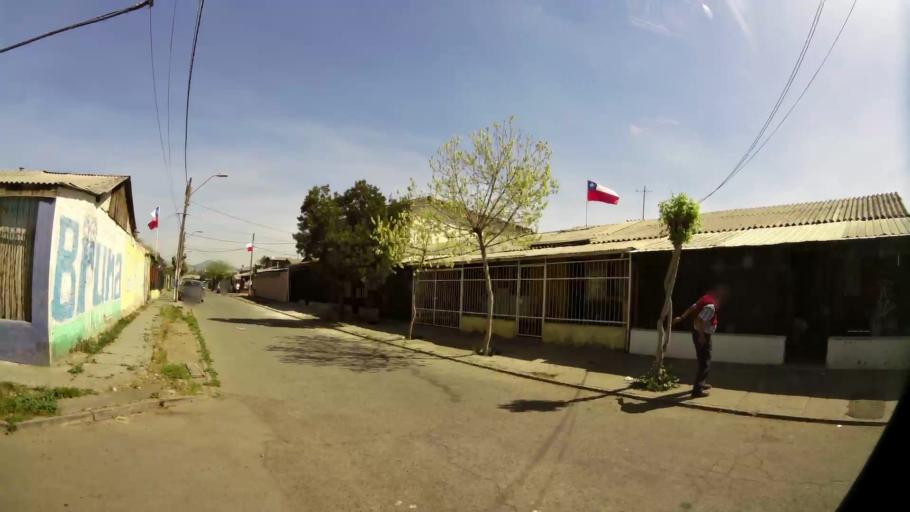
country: CL
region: Santiago Metropolitan
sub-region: Provincia de Maipo
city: San Bernardo
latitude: -33.5295
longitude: -70.7025
